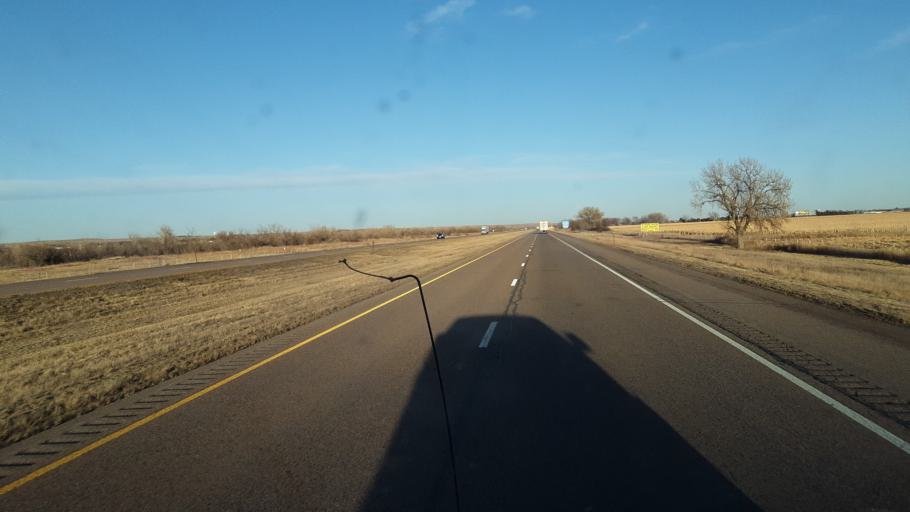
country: US
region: Nebraska
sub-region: Keith County
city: Ogallala
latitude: 41.1029
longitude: -101.7704
